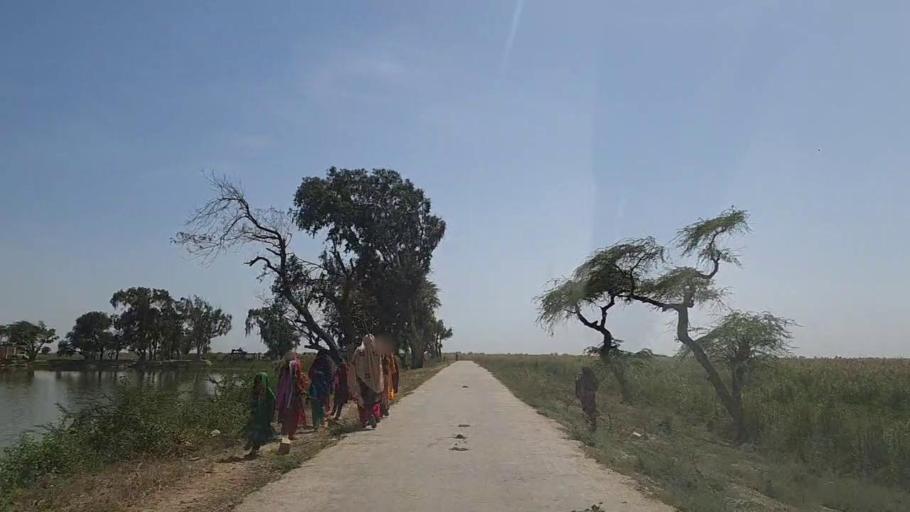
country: PK
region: Sindh
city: Gharo
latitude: 24.7890
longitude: 67.7526
